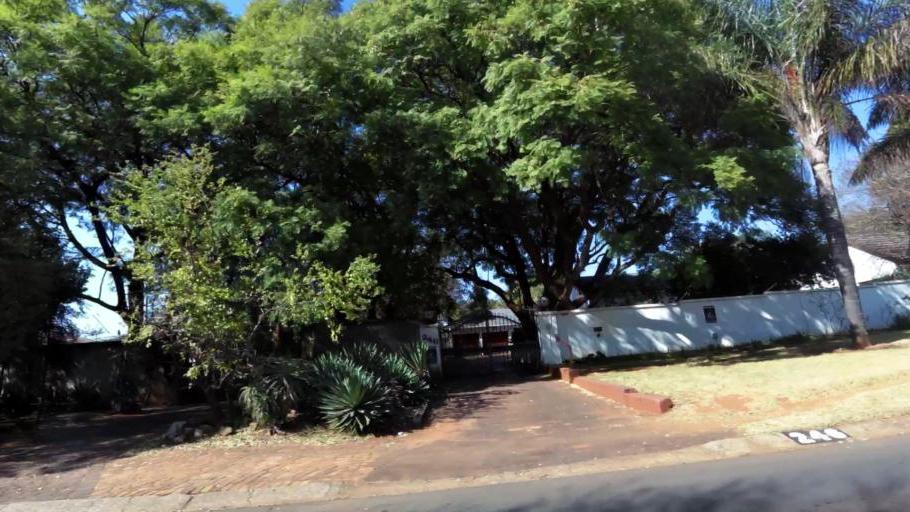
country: ZA
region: Gauteng
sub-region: City of Johannesburg Metropolitan Municipality
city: Roodepoort
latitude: -26.1238
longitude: 27.9491
